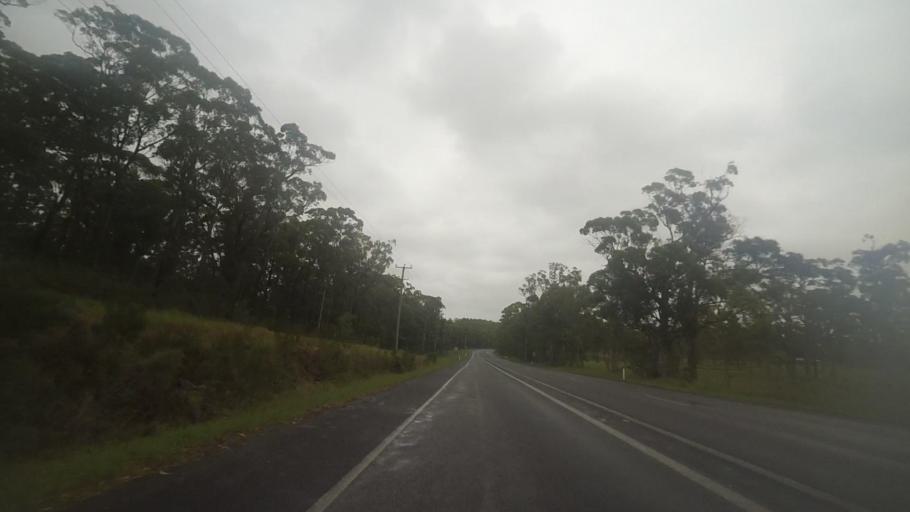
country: AU
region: New South Wales
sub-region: Port Stephens Shire
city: Port Stephens
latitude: -32.6455
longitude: 151.9823
